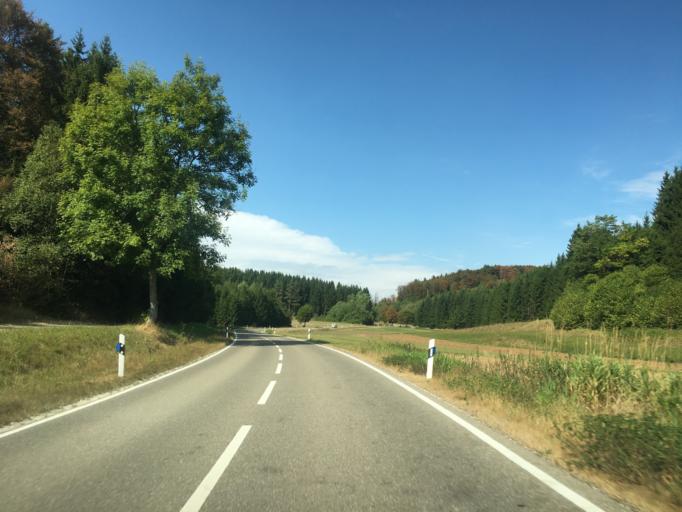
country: DE
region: Baden-Wuerttemberg
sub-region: Tuebingen Region
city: Trochtelfingen
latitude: 48.3708
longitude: 9.1992
